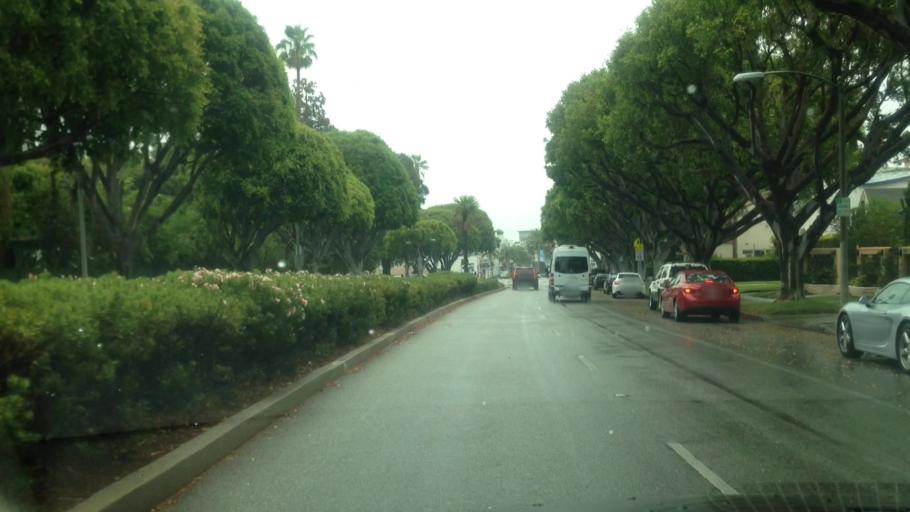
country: US
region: California
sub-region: Los Angeles County
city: Beverly Hills
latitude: 34.0723
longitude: -118.4062
